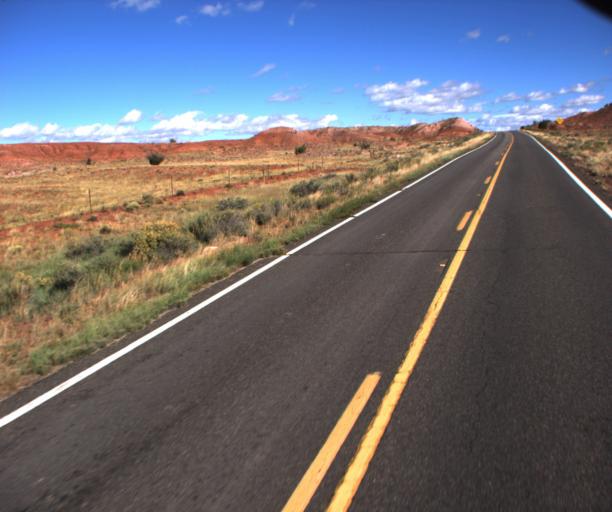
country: US
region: Arizona
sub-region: Apache County
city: Saint Johns
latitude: 34.7534
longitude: -109.2445
